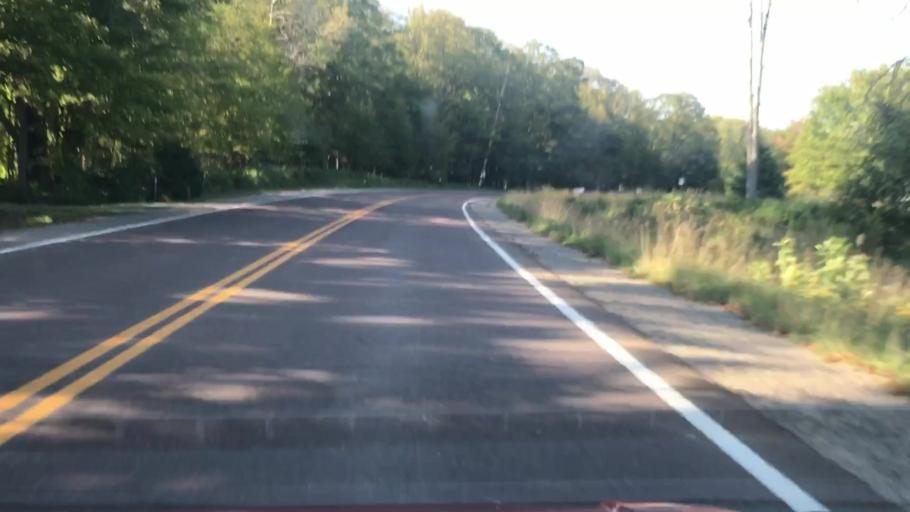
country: US
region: Michigan
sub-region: Chippewa County
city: Sault Ste. Marie
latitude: 46.2804
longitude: -84.0318
